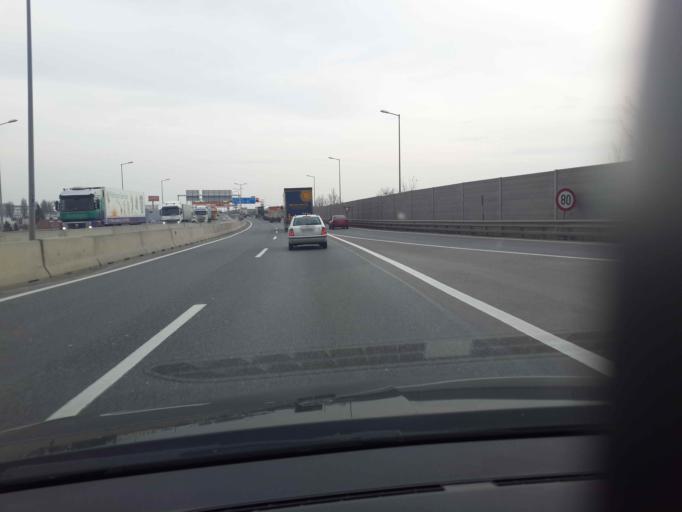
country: AT
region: Lower Austria
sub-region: Politischer Bezirk Wien-Umgebung
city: Schwechat
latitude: 48.1457
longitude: 16.4869
